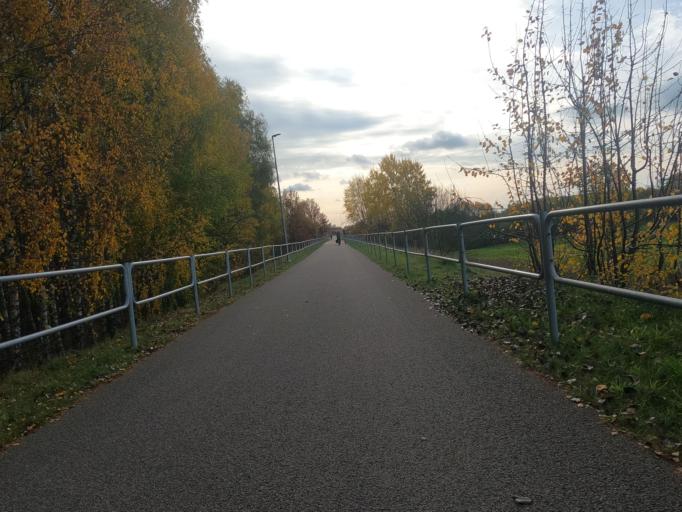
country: PL
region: Pomeranian Voivodeship
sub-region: Powiat starogardzki
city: Starogard Gdanski
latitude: 53.9871
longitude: 18.4703
